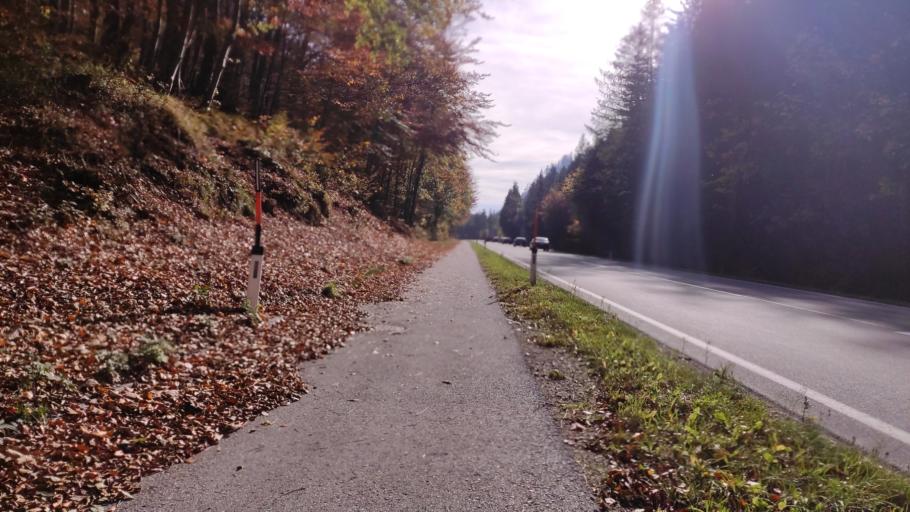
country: AT
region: Salzburg
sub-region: Politischer Bezirk Salzburg-Umgebung
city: Fuschl am See
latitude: 47.7972
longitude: 13.3238
